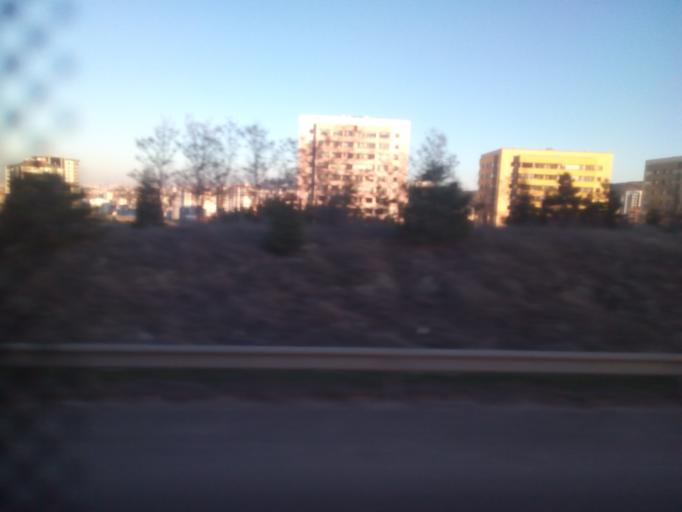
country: TR
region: Ankara
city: Etimesgut
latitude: 39.9022
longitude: 32.6245
